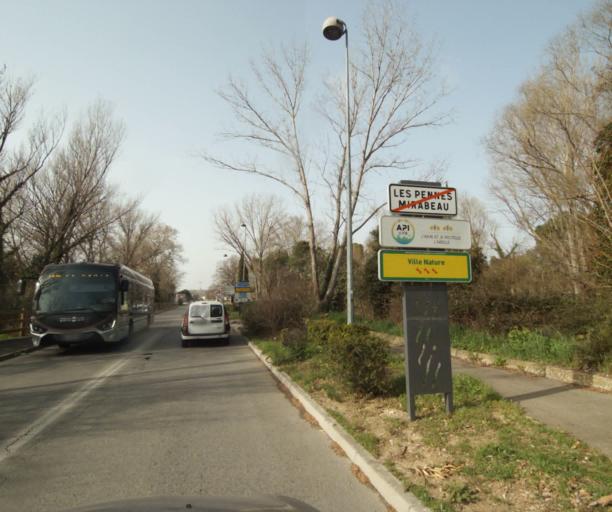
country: FR
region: Provence-Alpes-Cote d'Azur
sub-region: Departement des Bouches-du-Rhone
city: Les Pennes-Mirabeau
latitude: 43.4196
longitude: 5.2903
